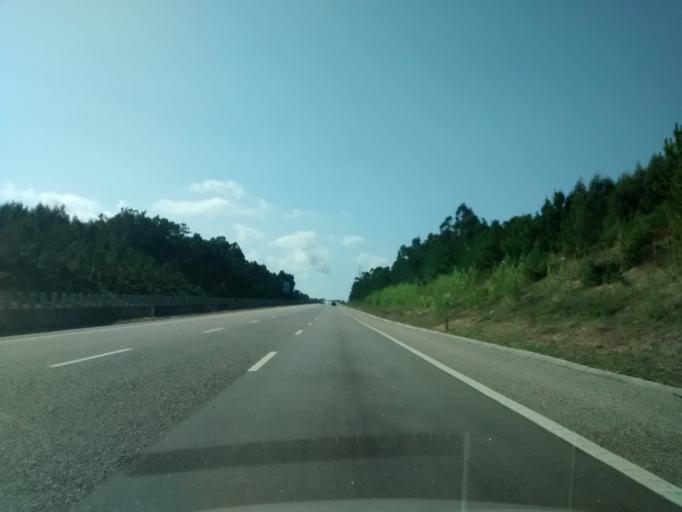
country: PT
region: Leiria
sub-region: Pombal
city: Lourical
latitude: 40.0078
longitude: -8.8020
